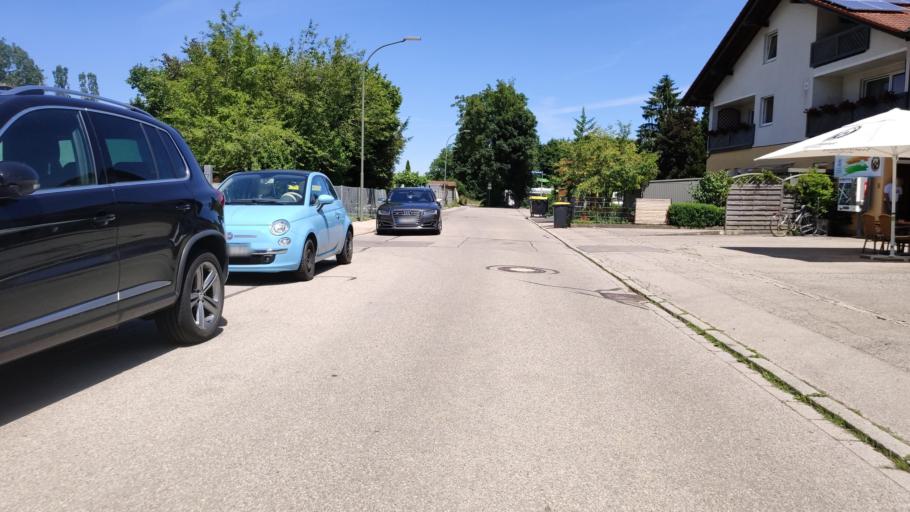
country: DE
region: Bavaria
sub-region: Swabia
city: Bad Worishofen
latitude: 48.0238
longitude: 10.5982
